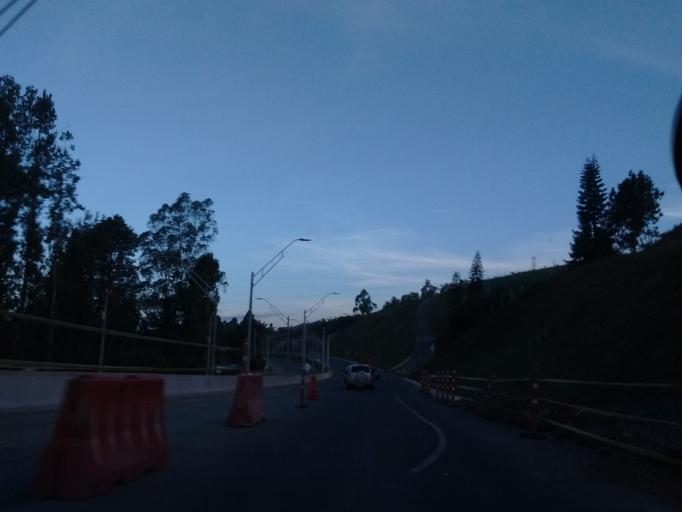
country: CO
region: Antioquia
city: Marinilla
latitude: 6.1632
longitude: -75.3195
